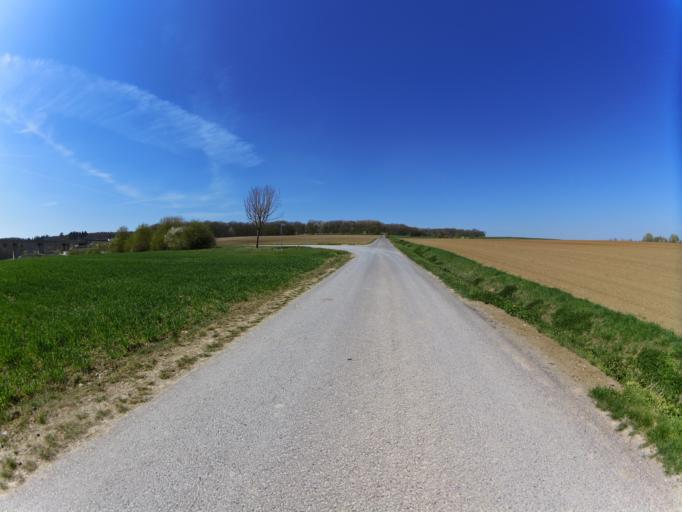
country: DE
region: Bavaria
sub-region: Regierungsbezirk Unterfranken
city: Estenfeld
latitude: 49.8595
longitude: 10.0018
